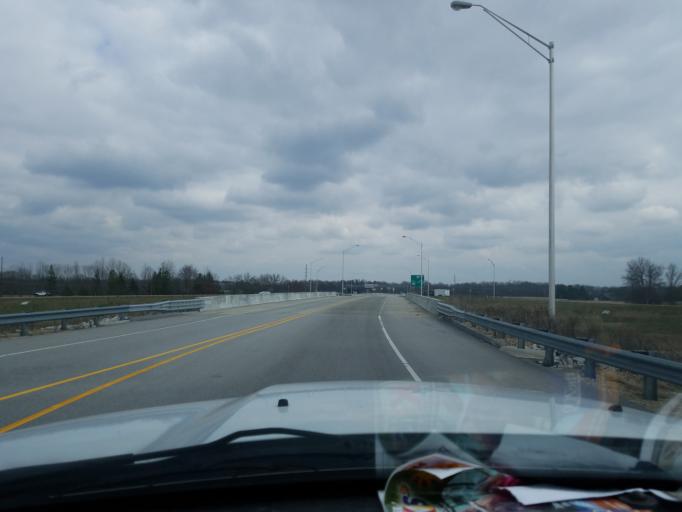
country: US
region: Indiana
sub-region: Vigo County
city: Terre Haute
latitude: 39.4136
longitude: -87.3361
